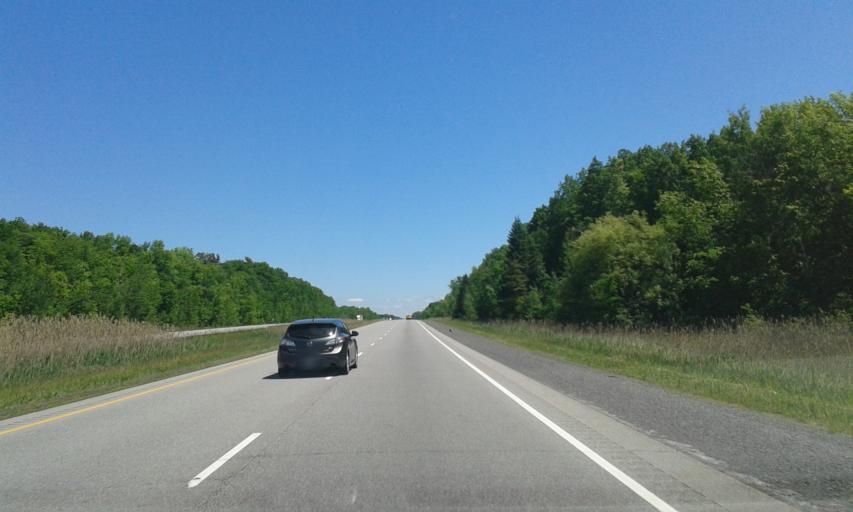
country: CA
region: Ontario
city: Prescott
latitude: 44.7854
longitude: -75.4452
